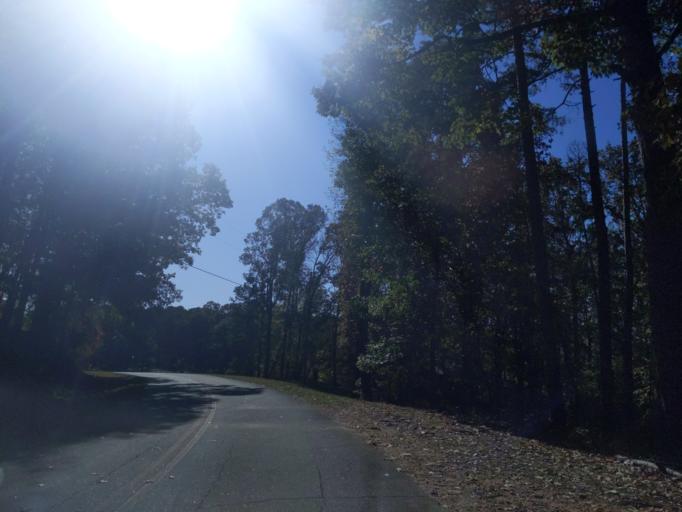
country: US
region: Georgia
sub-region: Franklin County
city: Gumlog
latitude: 34.4939
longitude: -83.0637
